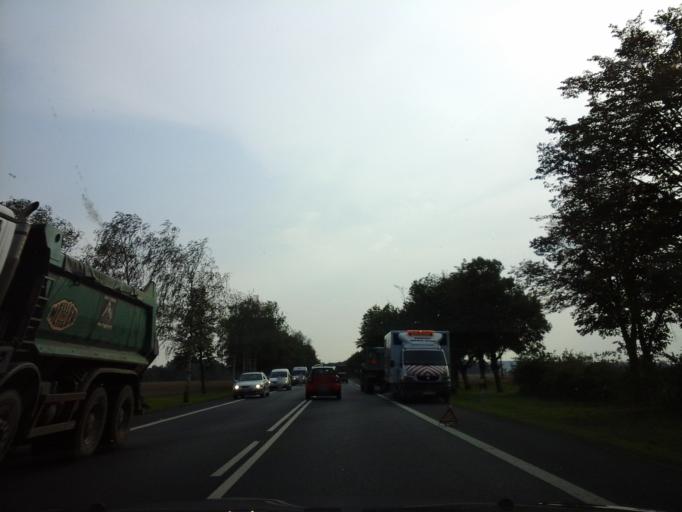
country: PL
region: Greater Poland Voivodeship
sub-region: Powiat koscianski
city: Smigiel
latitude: 52.0428
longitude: 16.5549
